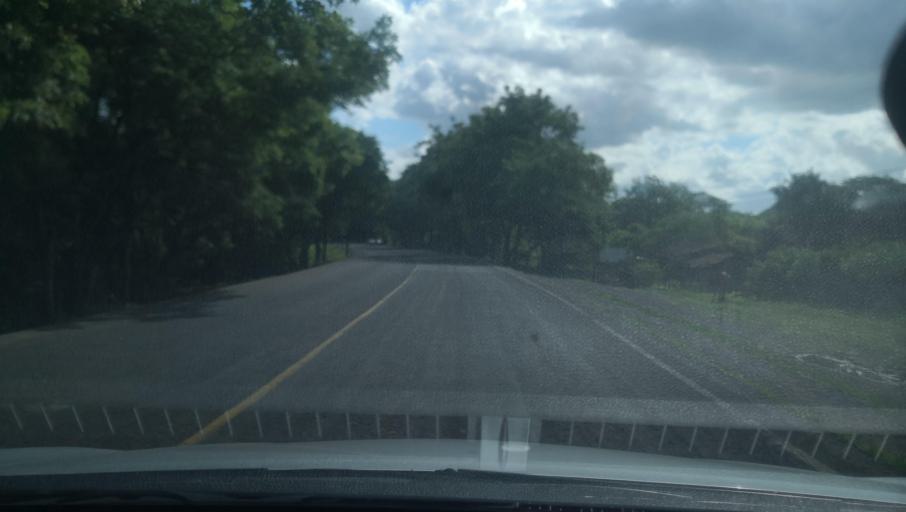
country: NI
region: Madriz
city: Somoto
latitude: 13.4688
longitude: -86.6301
